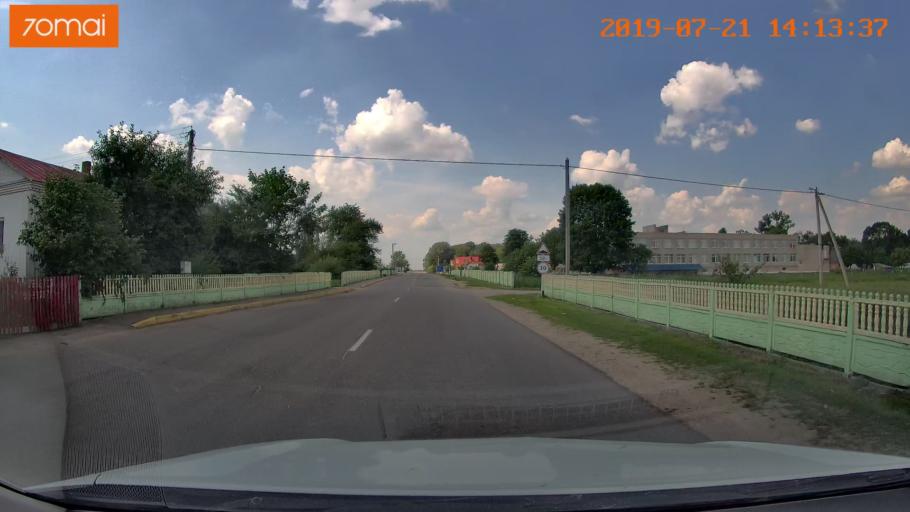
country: BY
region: Grodnenskaya
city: Karelichy
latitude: 53.6512
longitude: 26.1719
